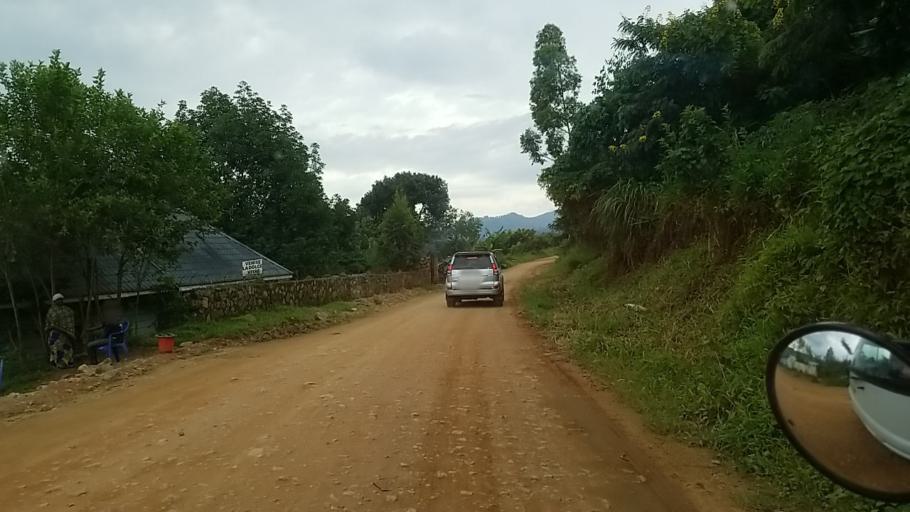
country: CD
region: Nord Kivu
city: Sake
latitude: -1.6739
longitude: 29.0183
